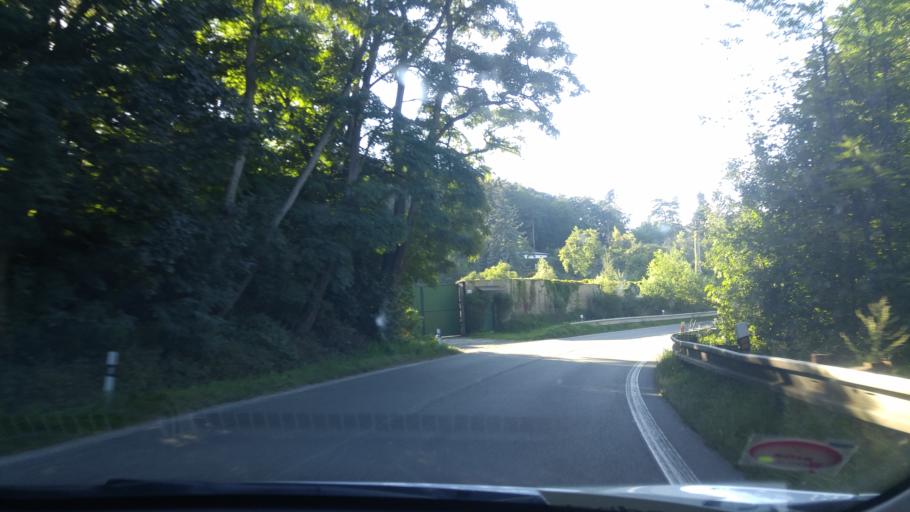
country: CZ
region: South Moravian
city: Troubsko
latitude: 49.2262
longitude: 16.5090
